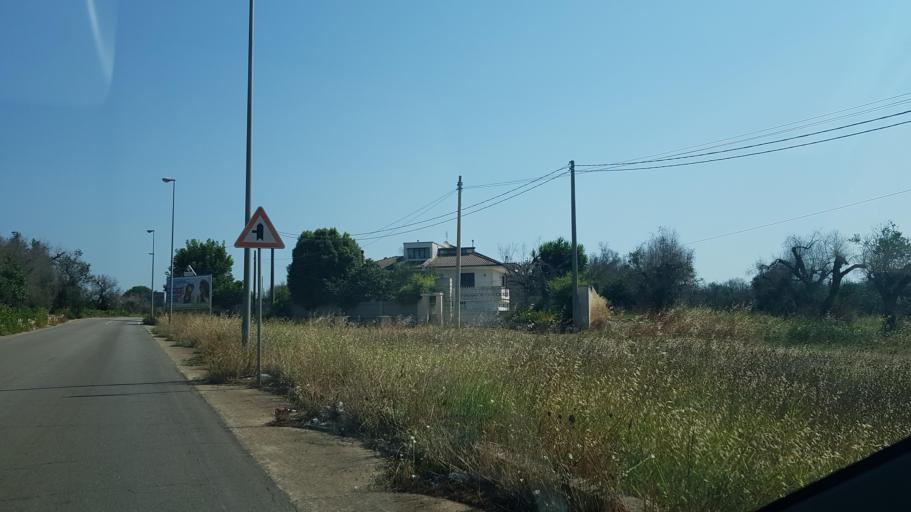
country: IT
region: Apulia
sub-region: Provincia di Lecce
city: Ruffano
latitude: 39.9941
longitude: 18.2629
